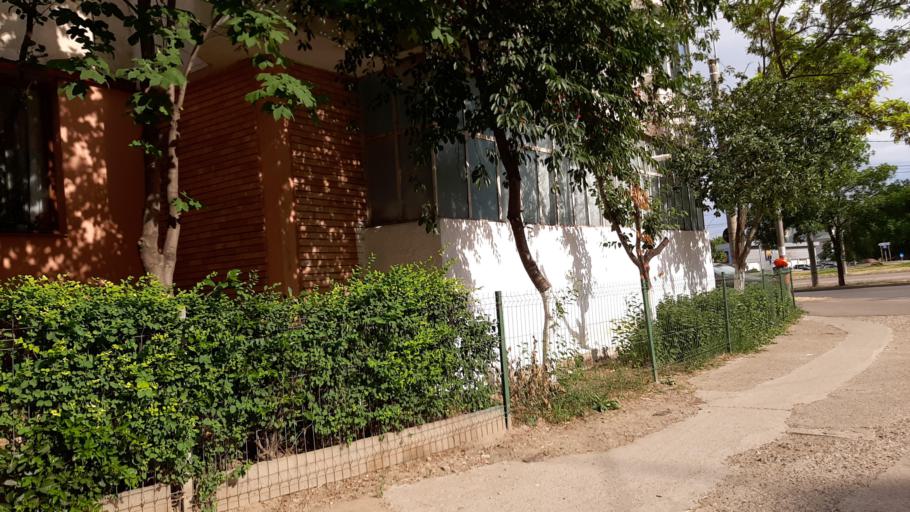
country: RO
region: Galati
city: Galati
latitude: 45.4412
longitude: 28.0286
